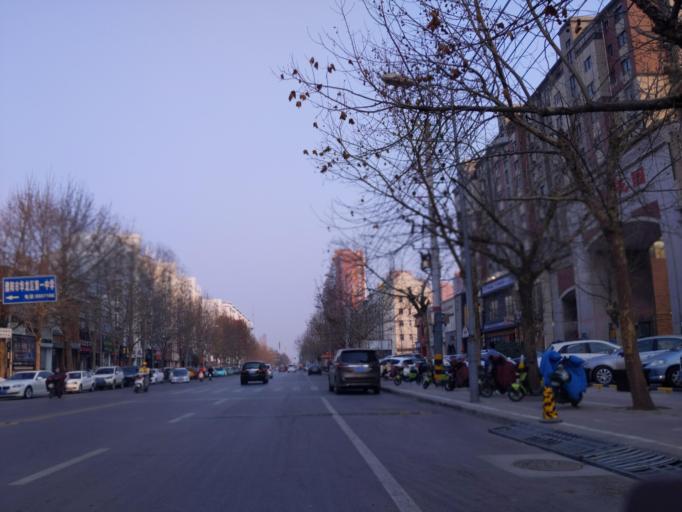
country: CN
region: Henan Sheng
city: Zhongyuanlu
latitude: 35.7743
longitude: 115.0612
